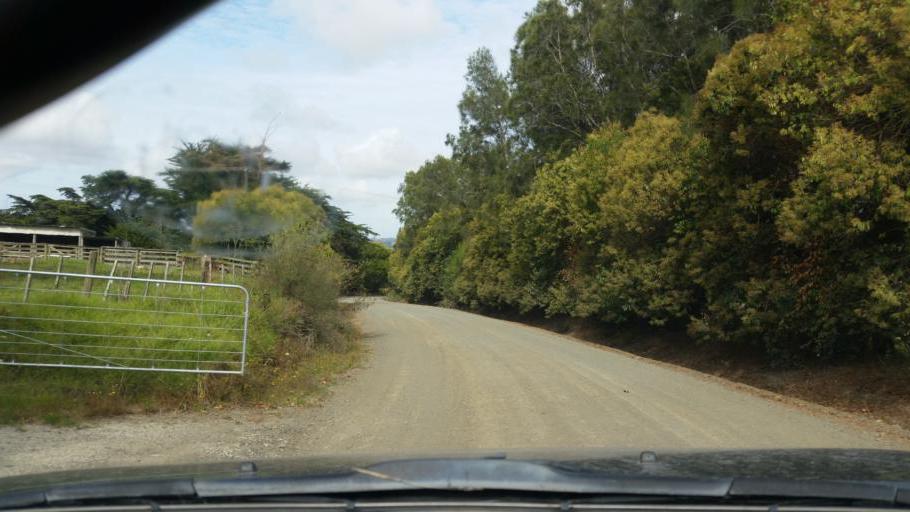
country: NZ
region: Northland
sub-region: Kaipara District
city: Dargaville
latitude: -35.9957
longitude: 173.9515
